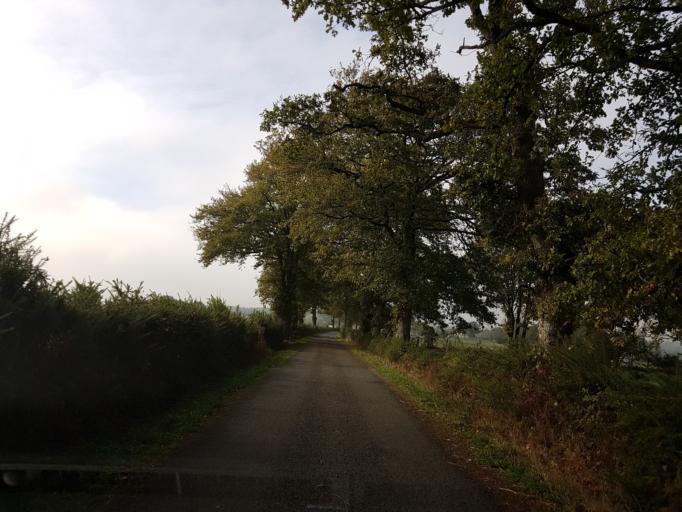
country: FR
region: Poitou-Charentes
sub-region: Departement de la Charente
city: Etagnac
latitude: 45.9114
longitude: 0.7413
